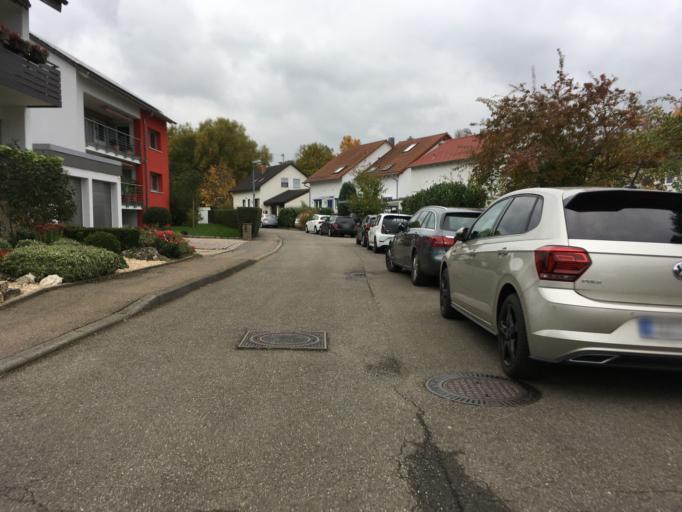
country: DE
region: Baden-Wuerttemberg
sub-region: Tuebingen Region
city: Gomaringen
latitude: 48.4495
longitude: 9.0984
